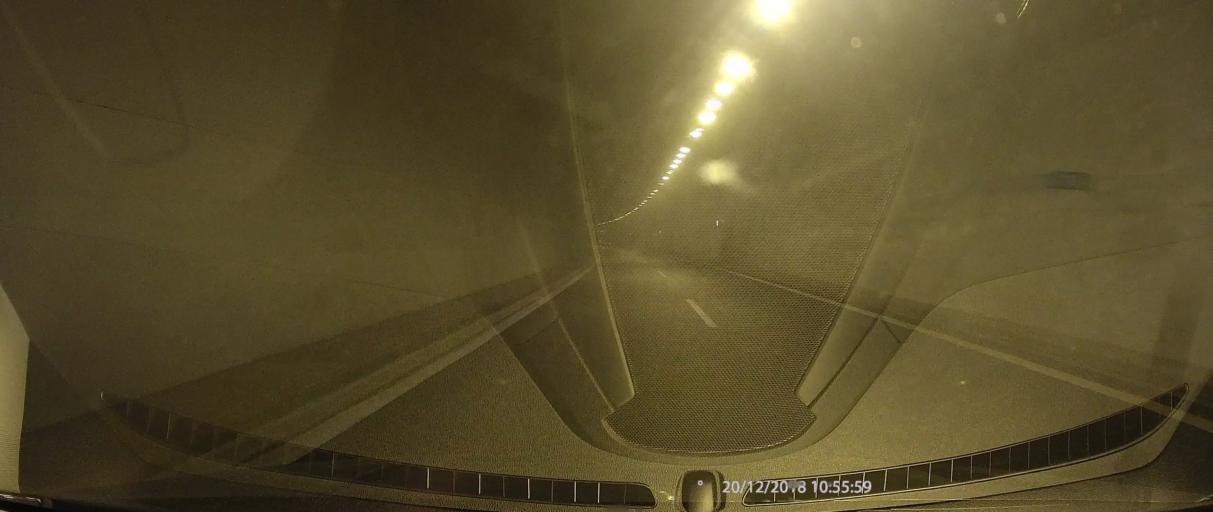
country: GR
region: Peloponnese
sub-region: Nomos Arkadias
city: Tripoli
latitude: 37.6572
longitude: 22.4696
